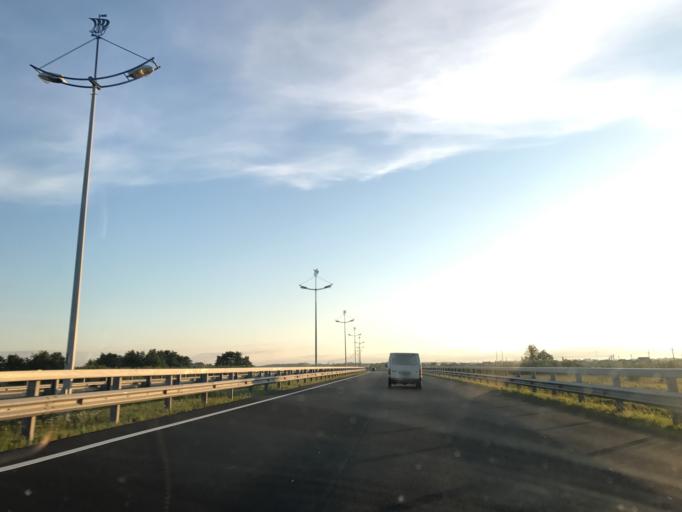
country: RU
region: Kaliningrad
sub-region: Zelenogradskiy Rayon
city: Zelenogradsk
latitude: 54.9233
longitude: 20.3836
